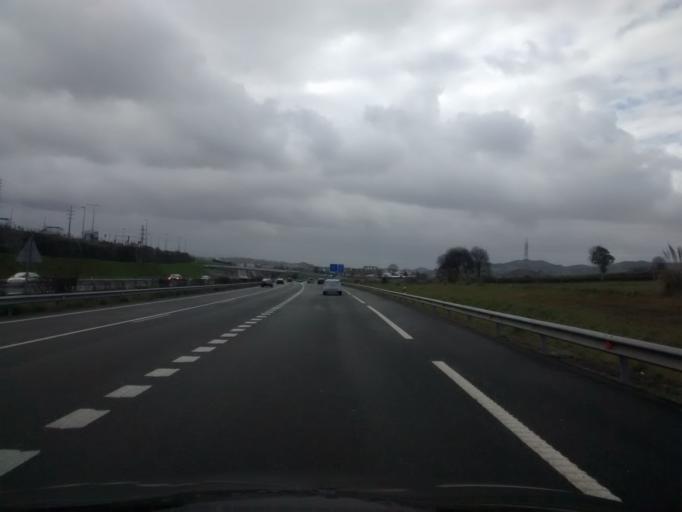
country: ES
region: Cantabria
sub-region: Provincia de Cantabria
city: Santa Cruz de Bezana
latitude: 43.4527
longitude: -3.8754
